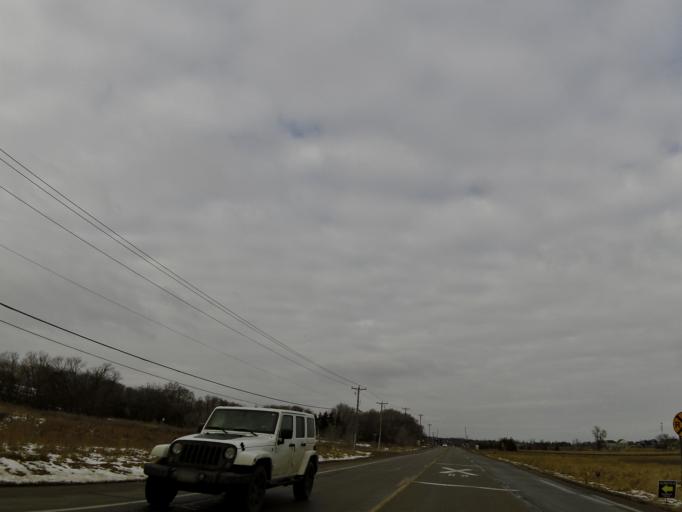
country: US
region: Minnesota
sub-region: Washington County
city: Bayport
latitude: 45.0062
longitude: -92.7940
